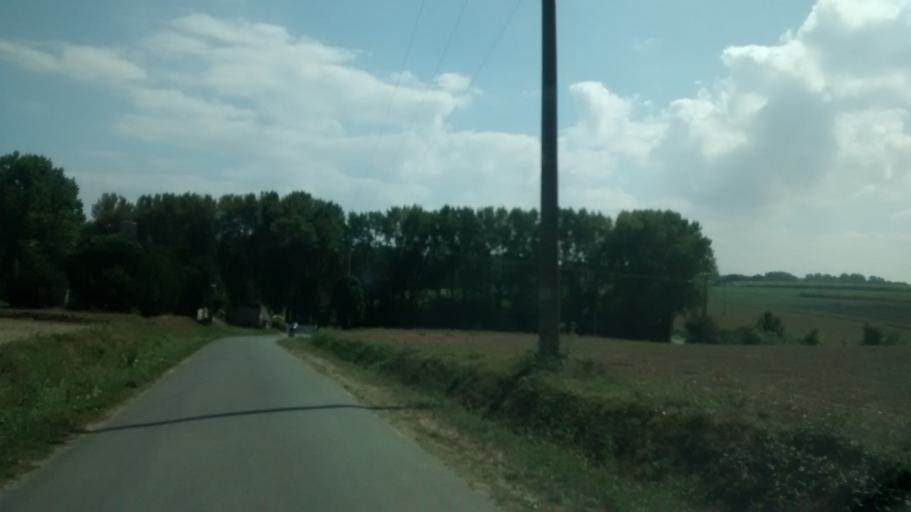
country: FR
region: Brittany
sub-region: Departement d'Ille-et-Vilaine
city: Saint-Coulomb
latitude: 48.6844
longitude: -1.8870
